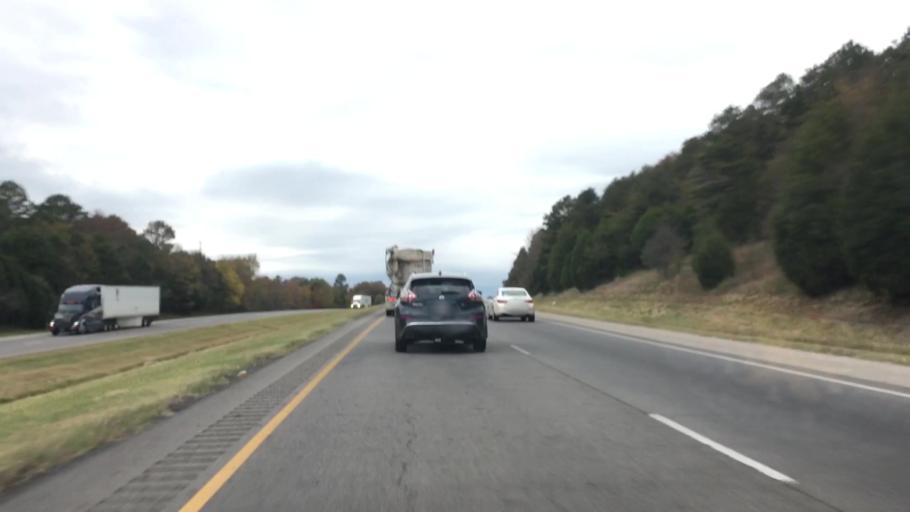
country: US
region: Arkansas
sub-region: Johnson County
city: Coal Hill
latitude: 35.5002
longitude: -93.7198
